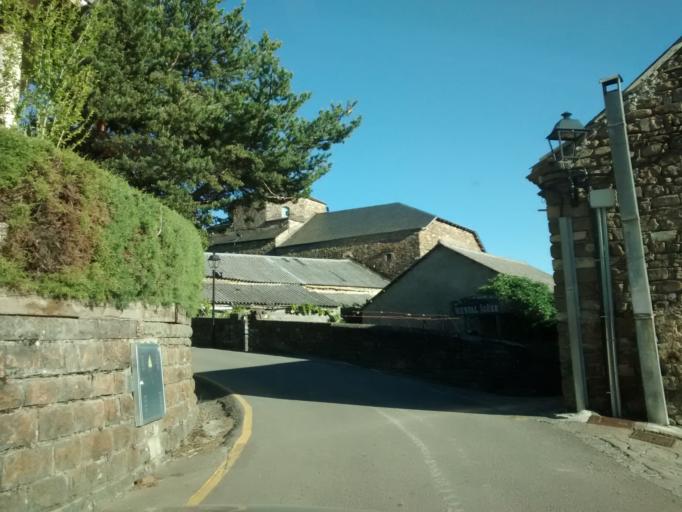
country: ES
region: Aragon
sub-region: Provincia de Huesca
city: Borau
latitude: 42.6801
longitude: -0.6205
